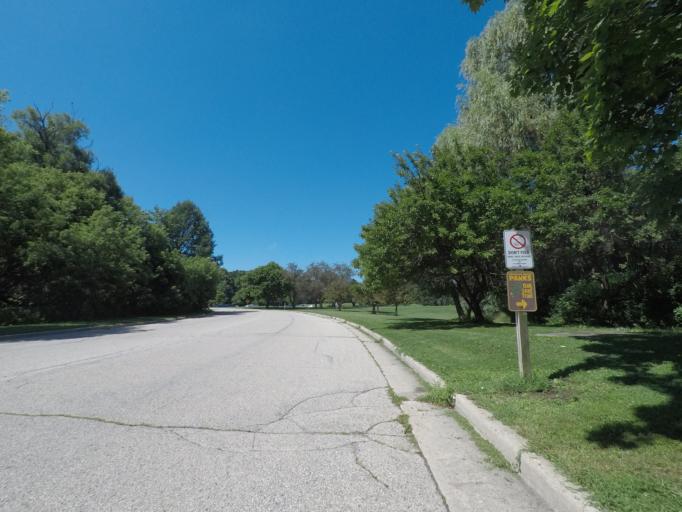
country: US
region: Wisconsin
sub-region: Waukesha County
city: Elm Grove
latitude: 43.0084
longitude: -88.0581
